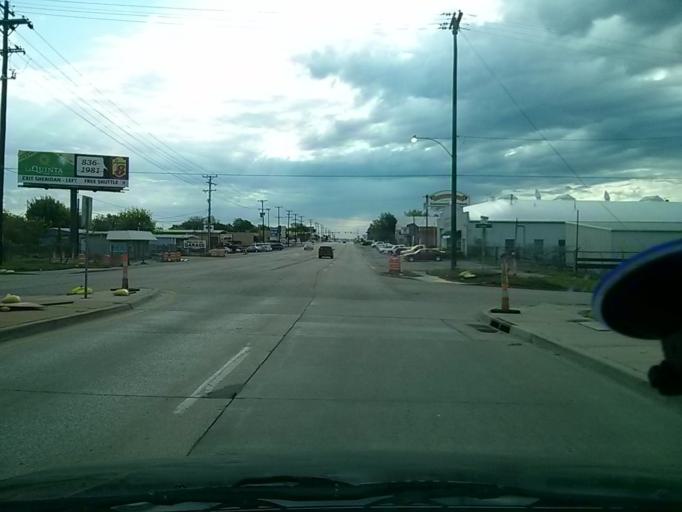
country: US
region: Oklahoma
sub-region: Tulsa County
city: Tulsa
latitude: 36.1608
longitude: -95.9140
